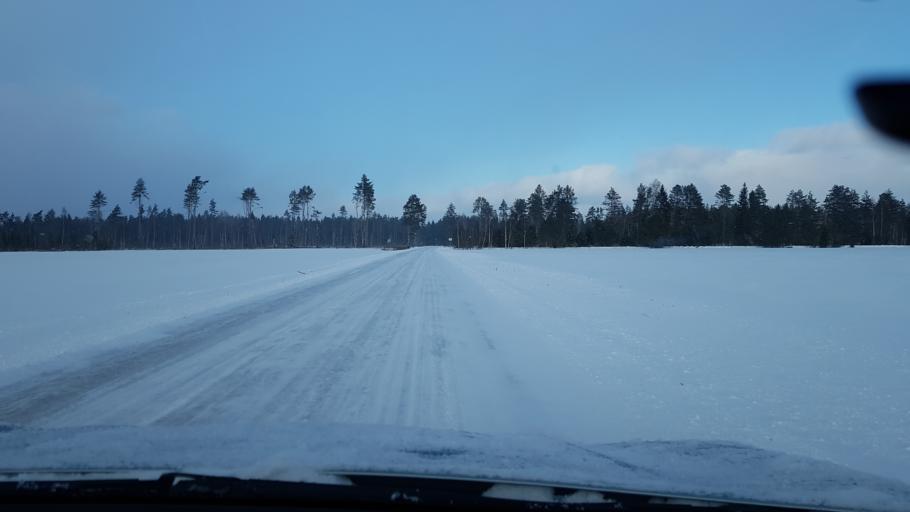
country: EE
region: Harju
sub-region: Nissi vald
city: Turba
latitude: 59.2033
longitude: 24.1402
